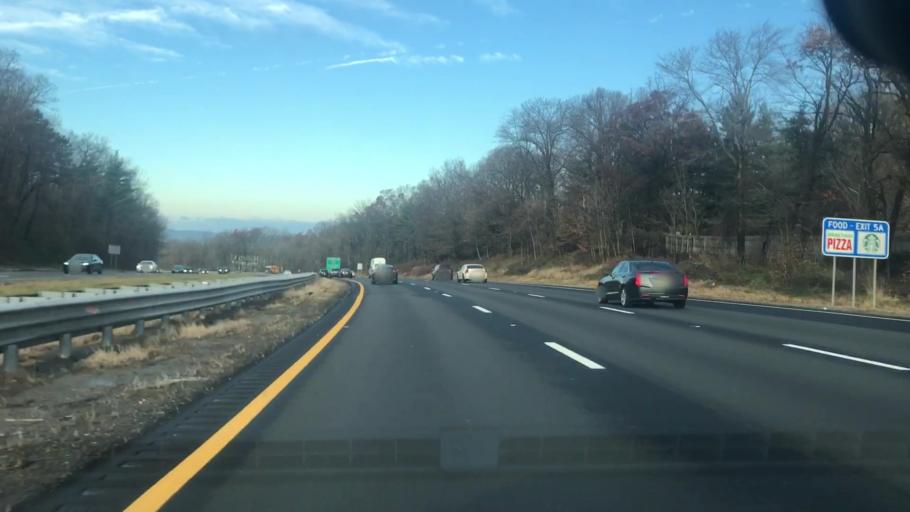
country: US
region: New Jersey
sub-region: Essex County
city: Roseland
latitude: 40.8092
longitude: -74.2903
